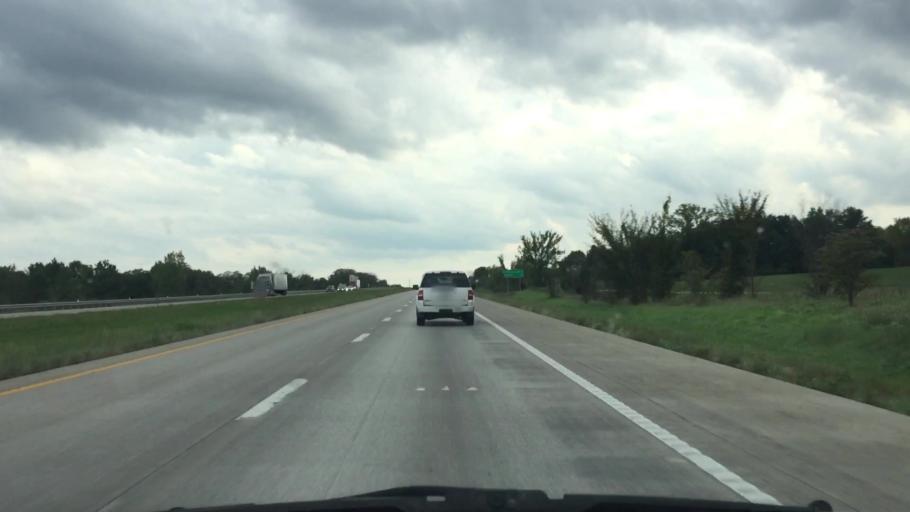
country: US
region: Missouri
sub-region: Clinton County
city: Cameron
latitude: 39.6548
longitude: -94.2391
